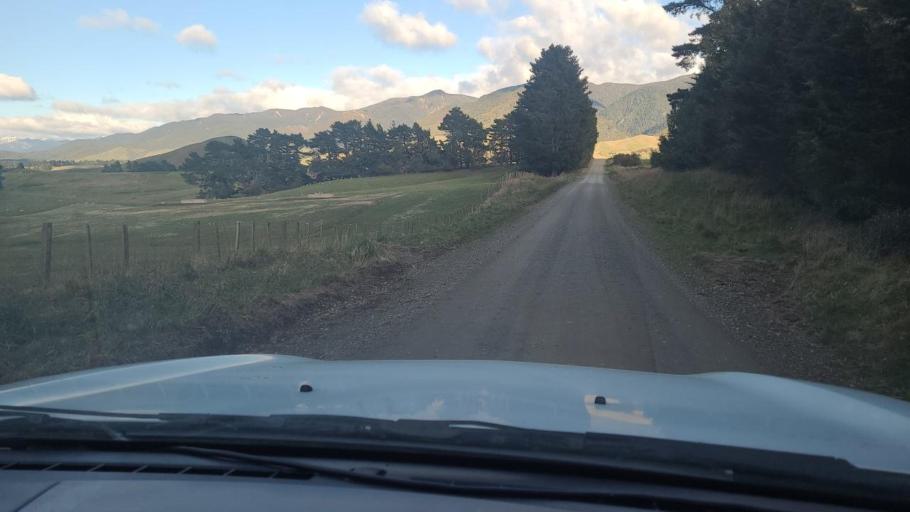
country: NZ
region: Hawke's Bay
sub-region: Hastings District
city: Hastings
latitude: -39.6348
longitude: 176.3388
